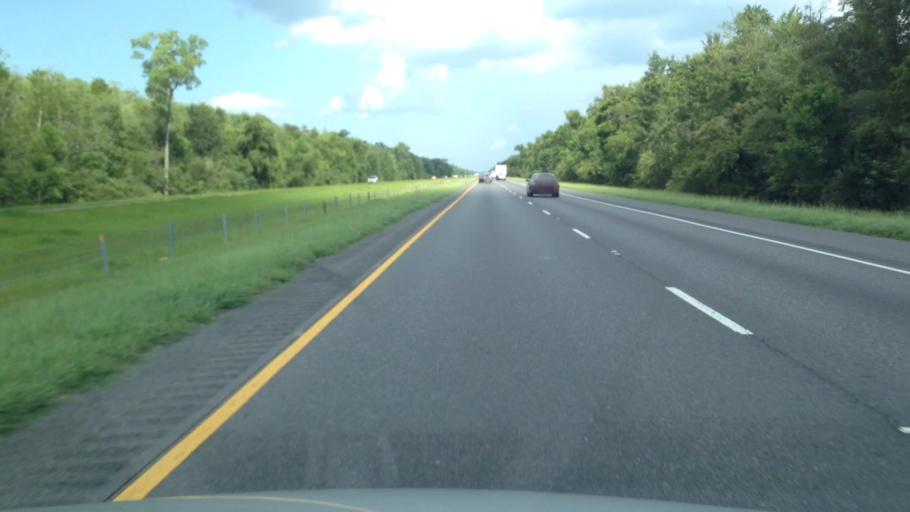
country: US
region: Louisiana
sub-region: Saint James Parish
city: Grand Point
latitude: 30.1404
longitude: -90.7491
